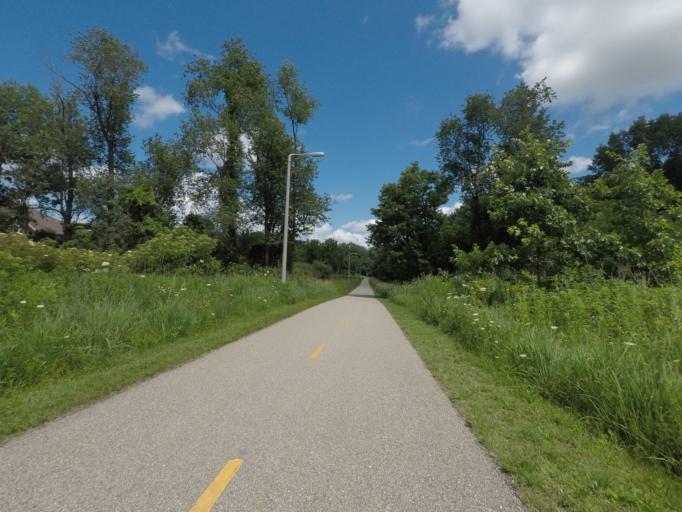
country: US
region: Wisconsin
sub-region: Dane County
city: Verona
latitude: 43.0236
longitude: -89.5288
